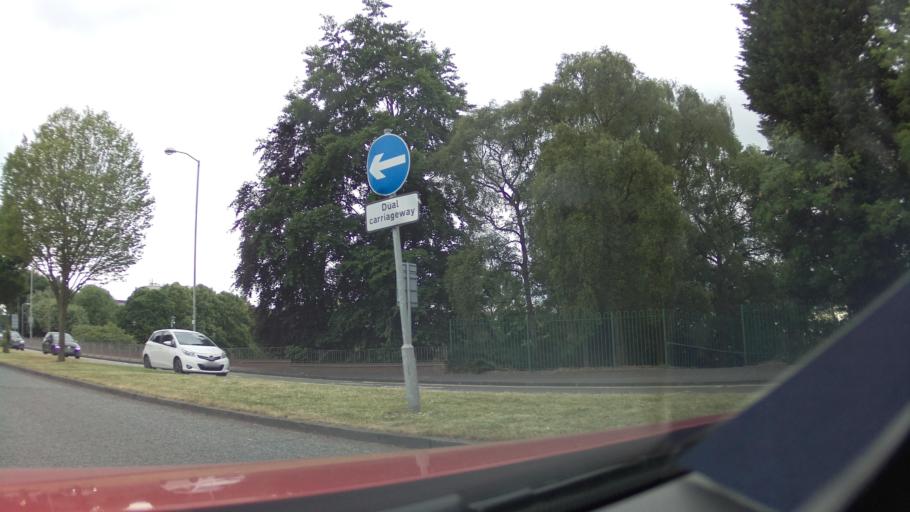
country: GB
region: England
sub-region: Wolverhampton
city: Wolverhampton
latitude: 52.5937
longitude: -2.1266
